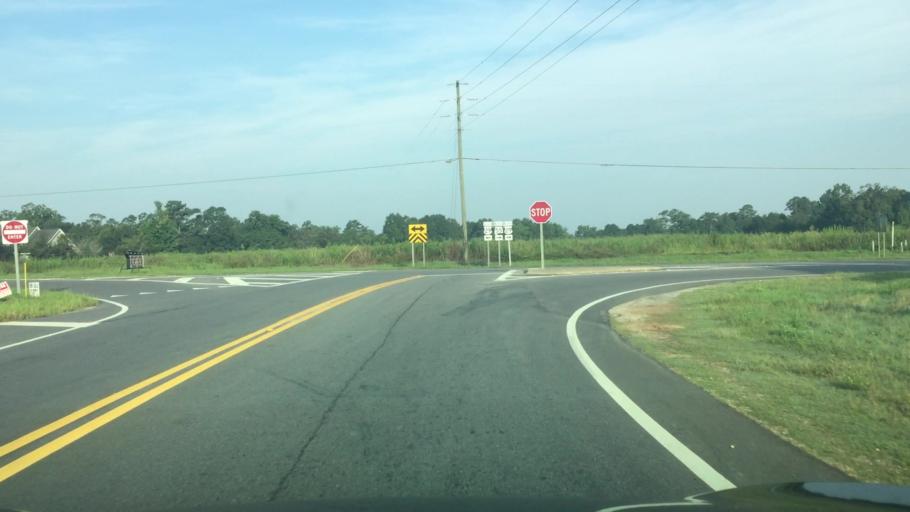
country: US
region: Alabama
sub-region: Covington County
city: Andalusia
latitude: 31.2780
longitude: -86.5057
